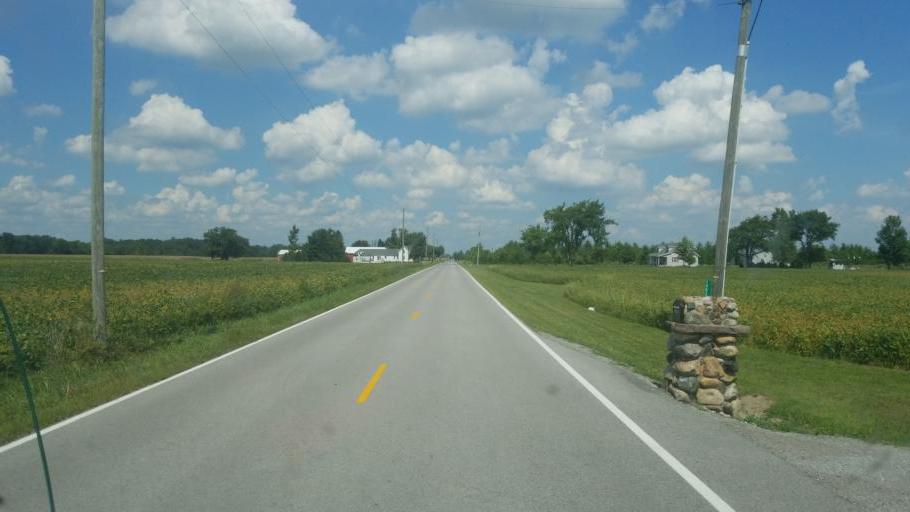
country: US
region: Ohio
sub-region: Hancock County
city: Arlington
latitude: 40.8797
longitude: -83.7272
